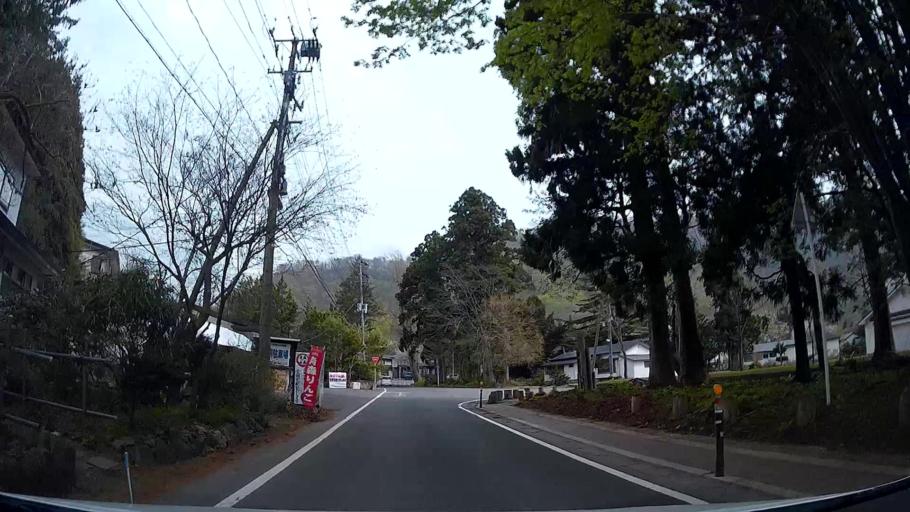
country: JP
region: Akita
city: Hanawa
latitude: 40.4260
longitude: 140.8965
